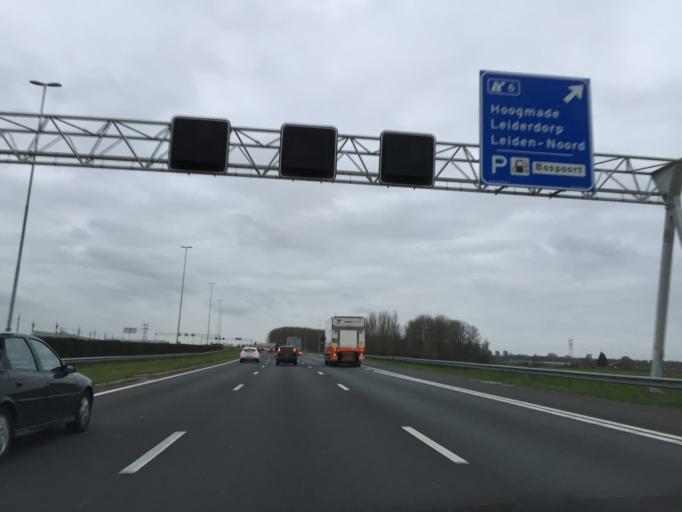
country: NL
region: South Holland
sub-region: Gemeente Leiderdorp
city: Leiderdorp
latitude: 52.1712
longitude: 4.5675
